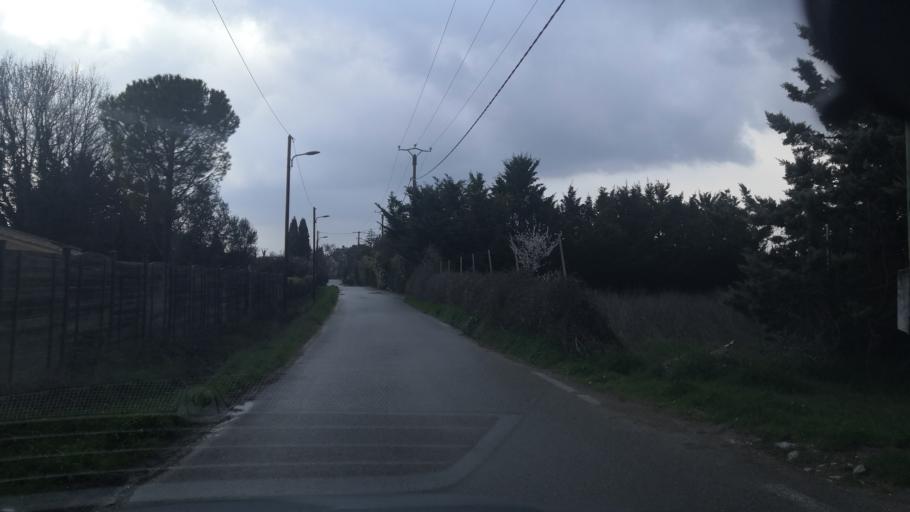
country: FR
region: Provence-Alpes-Cote d'Azur
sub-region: Departement des Bouches-du-Rhone
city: Aix-en-Provence
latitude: 43.5582
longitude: 5.4179
